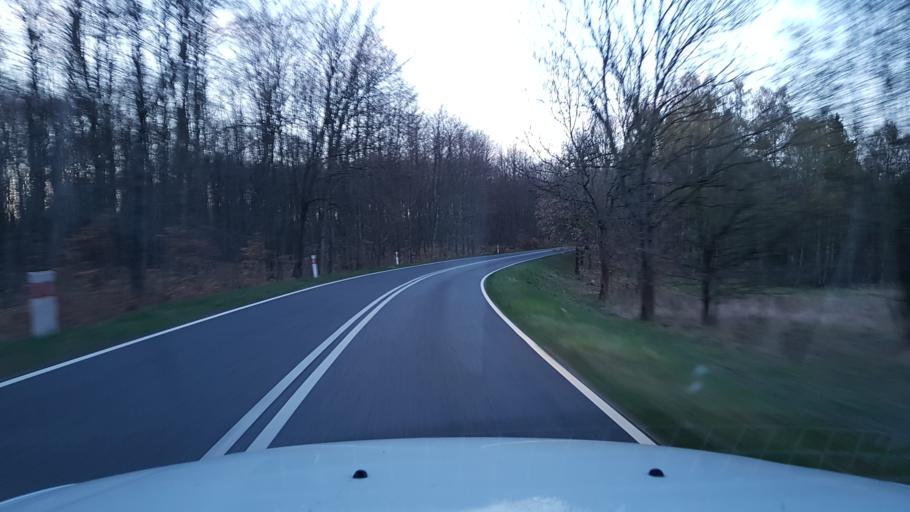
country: PL
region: West Pomeranian Voivodeship
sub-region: Powiat stargardzki
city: Insko
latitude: 53.4852
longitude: 15.5799
